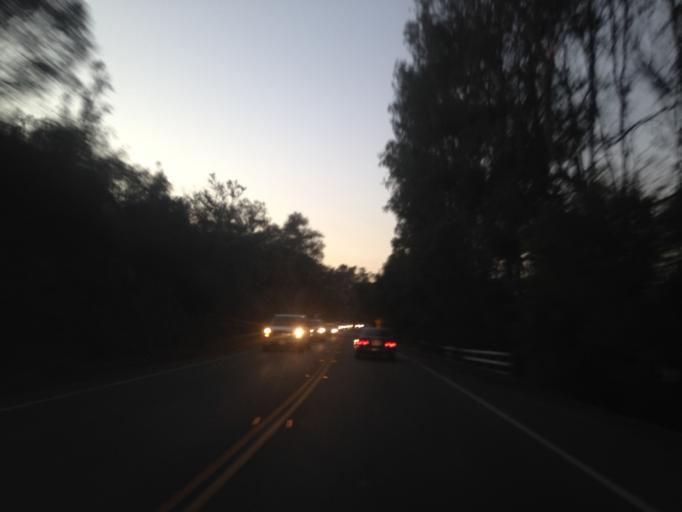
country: US
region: California
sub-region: San Diego County
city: Bonsall
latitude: 33.2561
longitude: -117.2095
